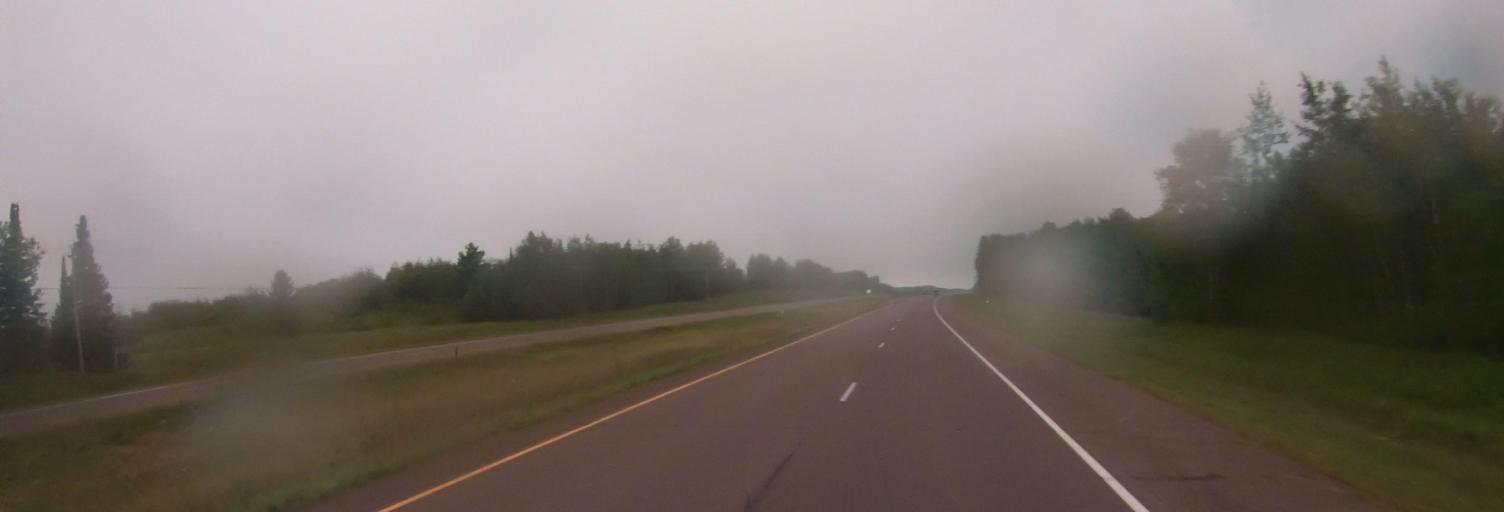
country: US
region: Minnesota
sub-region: Carlton County
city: Cloquet
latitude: 46.9141
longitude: -92.4702
